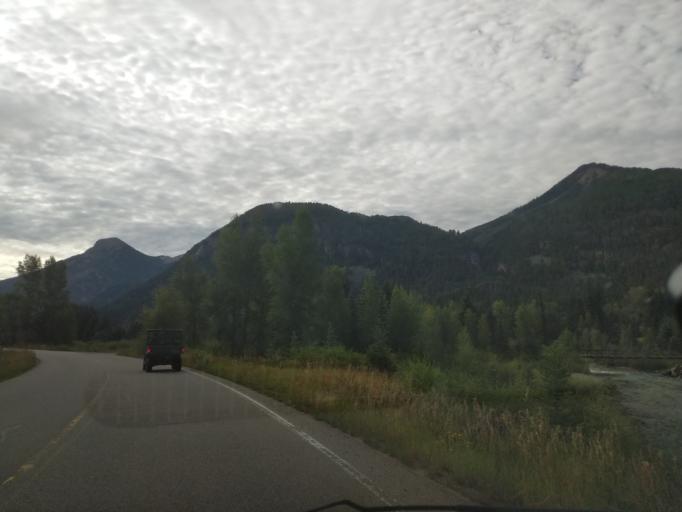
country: US
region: Colorado
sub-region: Gunnison County
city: Crested Butte
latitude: 39.0763
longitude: -107.2223
